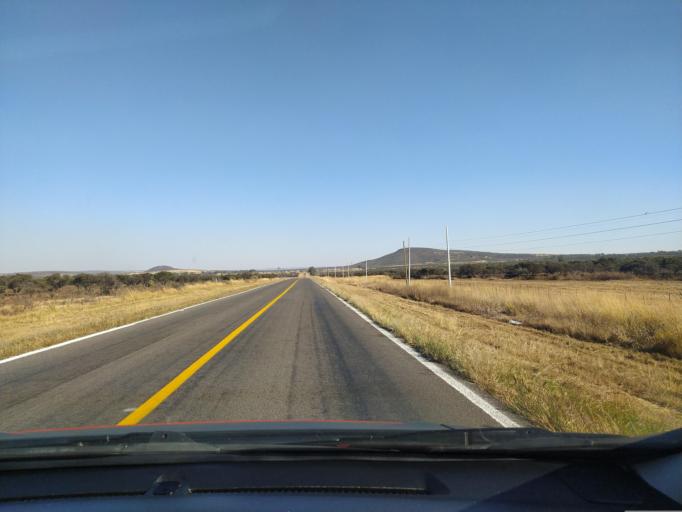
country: MX
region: Jalisco
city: San Miguel el Alto
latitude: 21.0170
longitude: -102.4911
